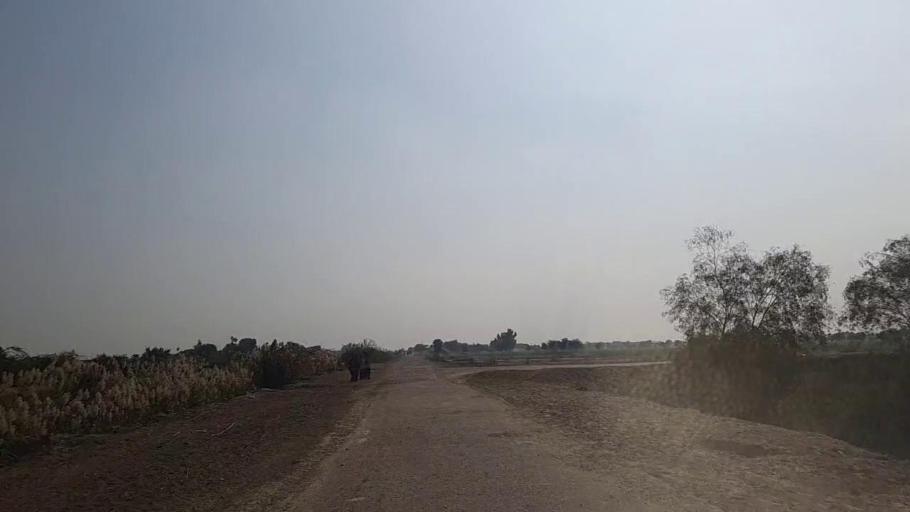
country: PK
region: Sindh
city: Daur
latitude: 26.4699
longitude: 68.4664
